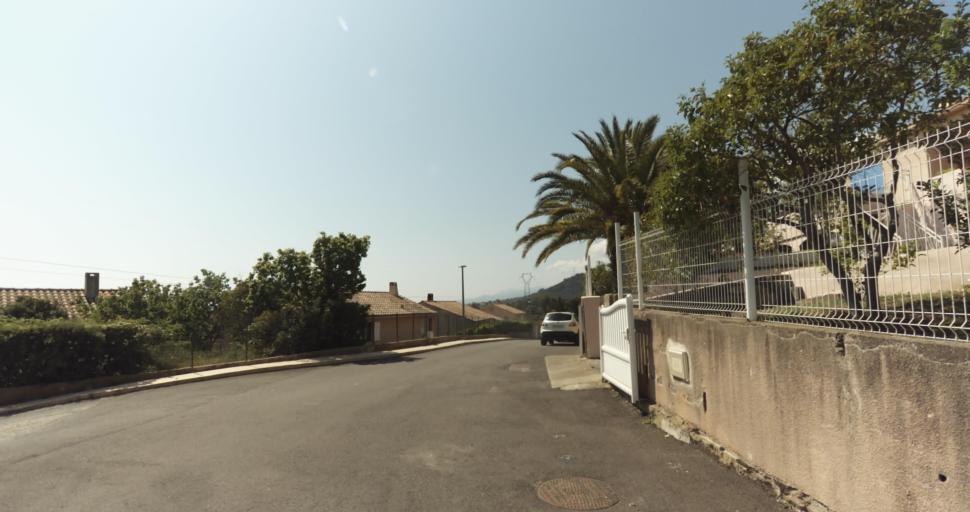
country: FR
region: Corsica
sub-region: Departement de la Haute-Corse
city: Biguglia
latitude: 42.6193
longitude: 9.4237
